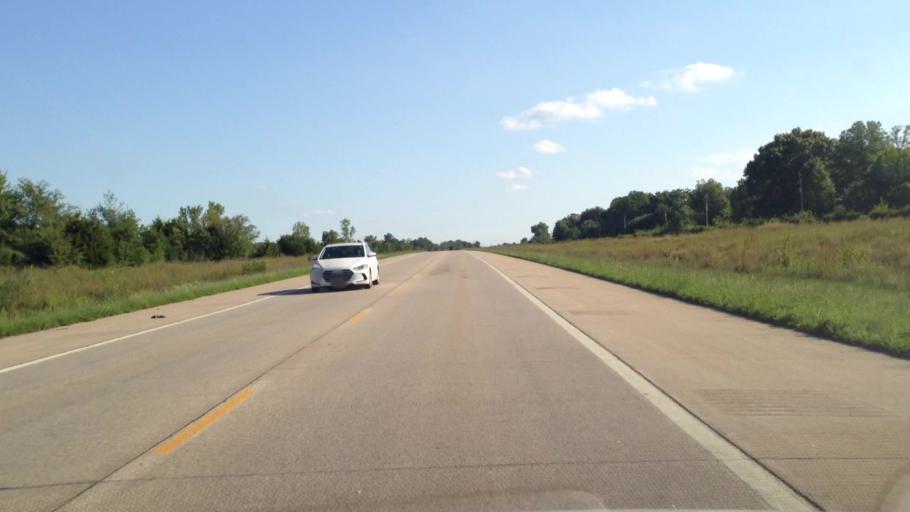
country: US
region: Kansas
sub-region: Crawford County
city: Arma
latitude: 37.5658
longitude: -94.7047
